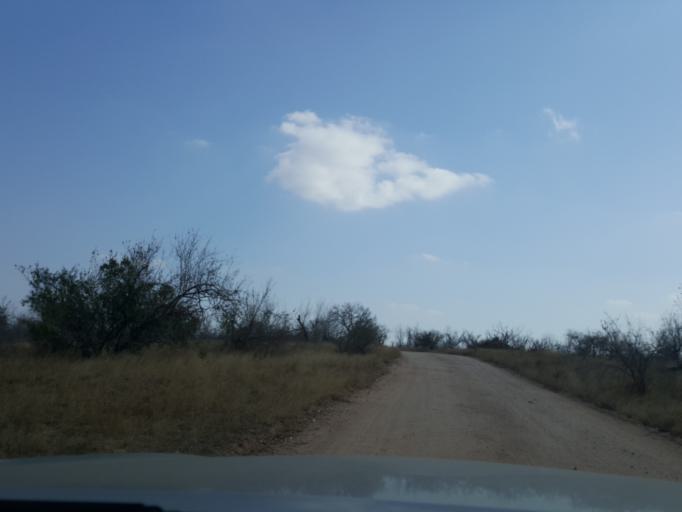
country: ZA
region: Mpumalanga
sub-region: Ehlanzeni District
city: Komatipoort
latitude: -25.2935
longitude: 31.7620
